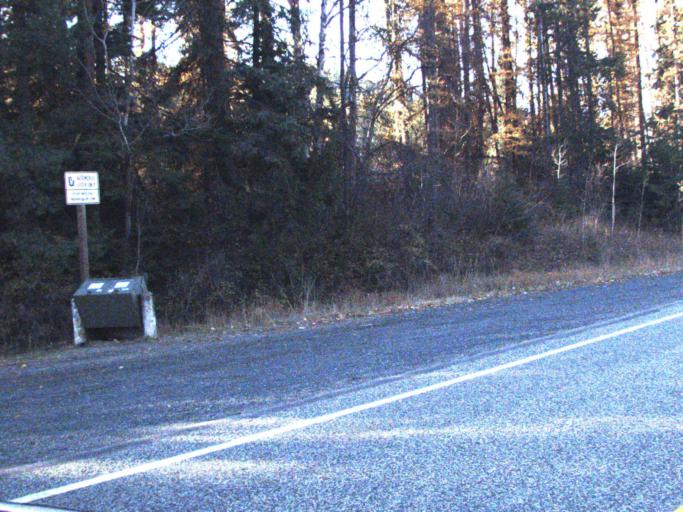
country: CA
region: British Columbia
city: Rossland
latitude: 48.9776
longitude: -117.8210
